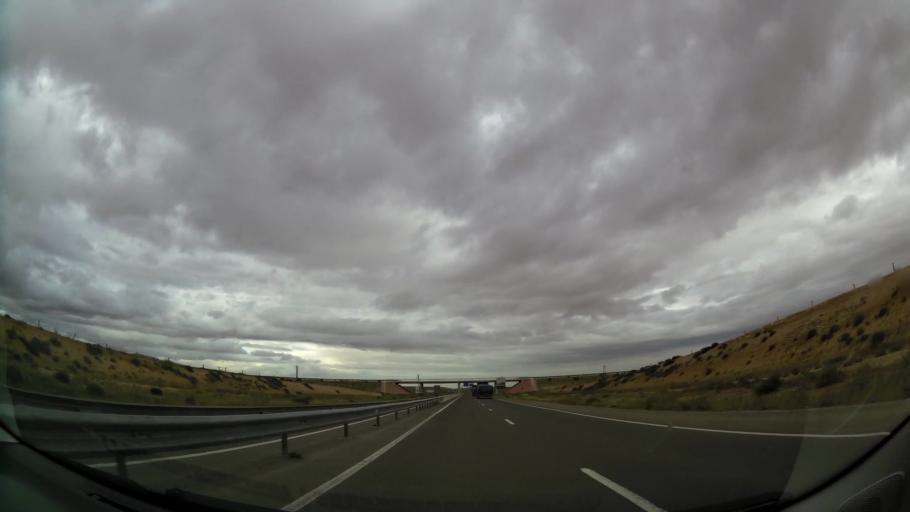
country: MA
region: Taza-Al Hoceima-Taounate
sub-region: Taza
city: Taza
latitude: 34.3094
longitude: -3.7346
